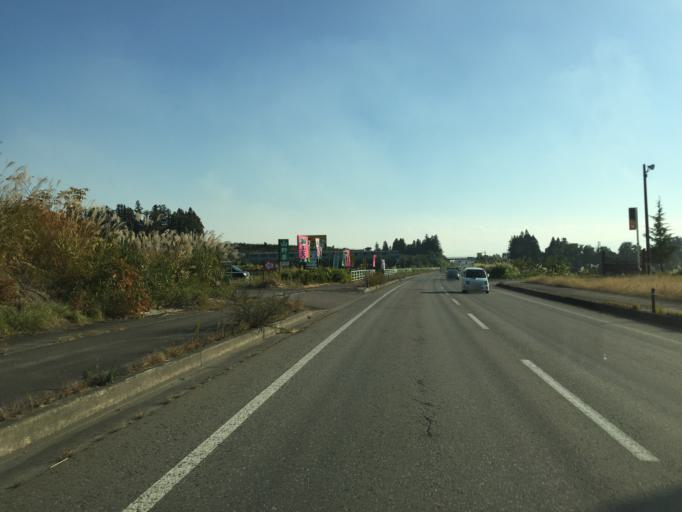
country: JP
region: Fukushima
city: Kitakata
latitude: 37.6900
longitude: 139.8903
